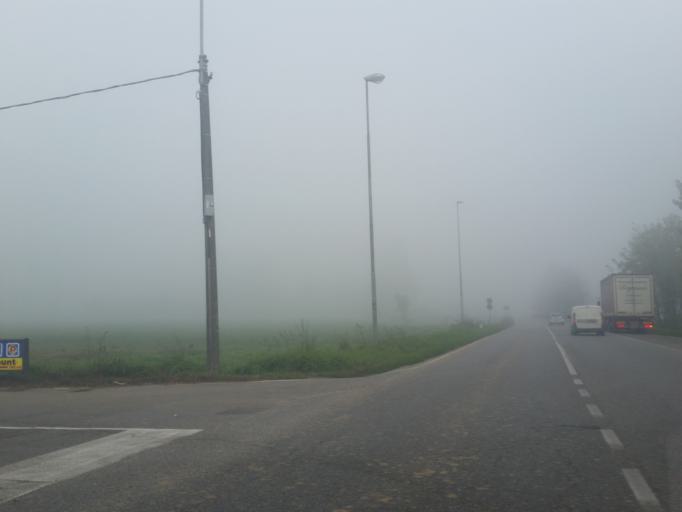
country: IT
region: Lombardy
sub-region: Provincia di Brescia
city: Dello
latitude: 45.4115
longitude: 10.0774
